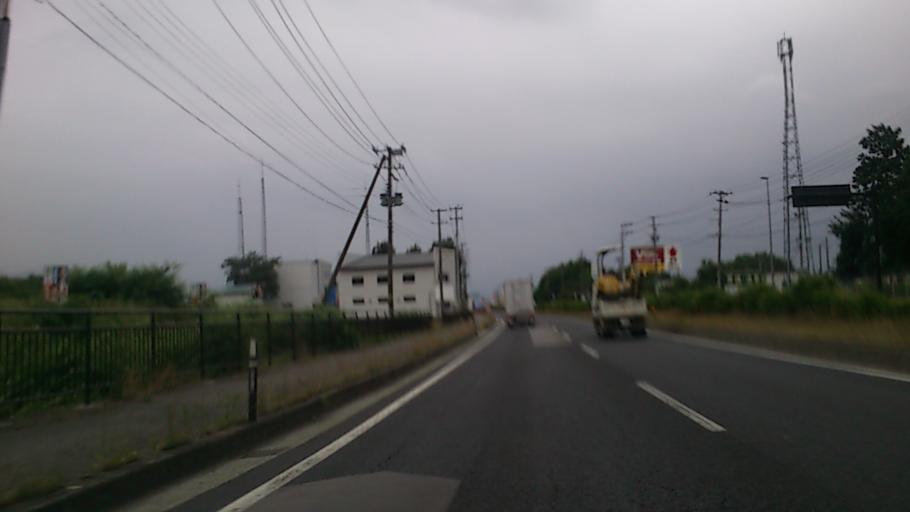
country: JP
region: Yamagata
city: Tendo
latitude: 38.3396
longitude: 140.3724
